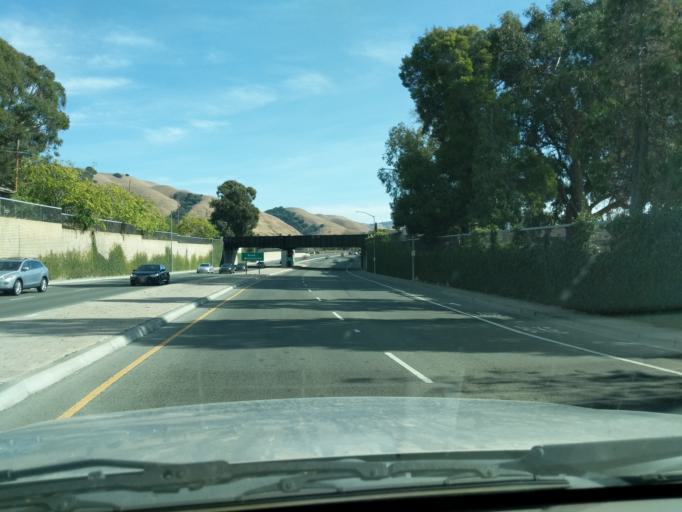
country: US
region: California
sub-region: Alameda County
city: Fremont
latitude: 37.5782
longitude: -121.9749
